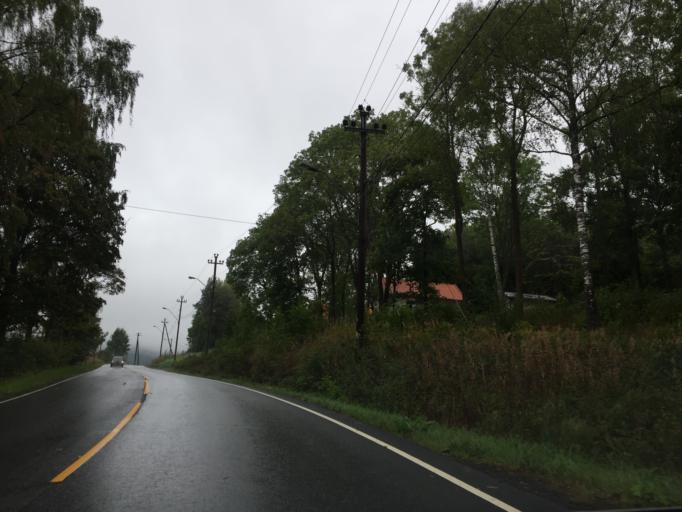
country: NO
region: Akershus
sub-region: Baerum
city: Lysaker
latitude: 59.9781
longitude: 10.6231
